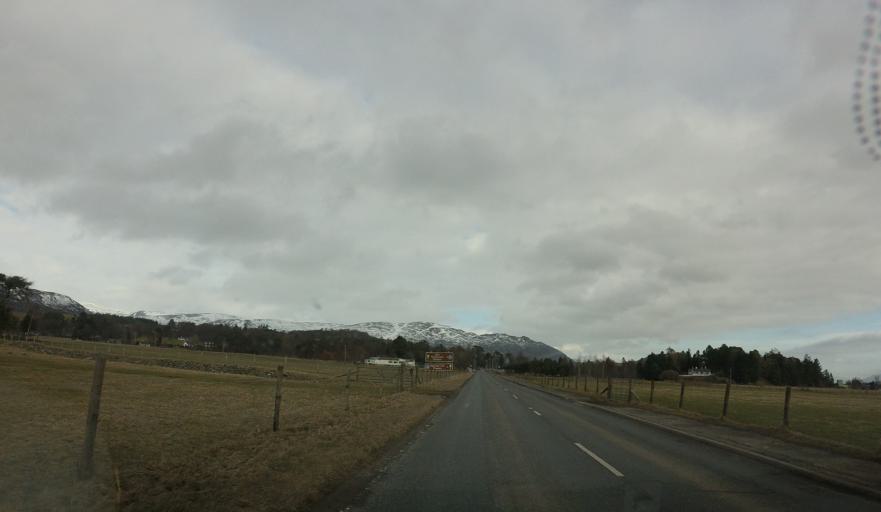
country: GB
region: Scotland
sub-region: Highland
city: Kingussie
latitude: 57.0577
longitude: -4.1298
